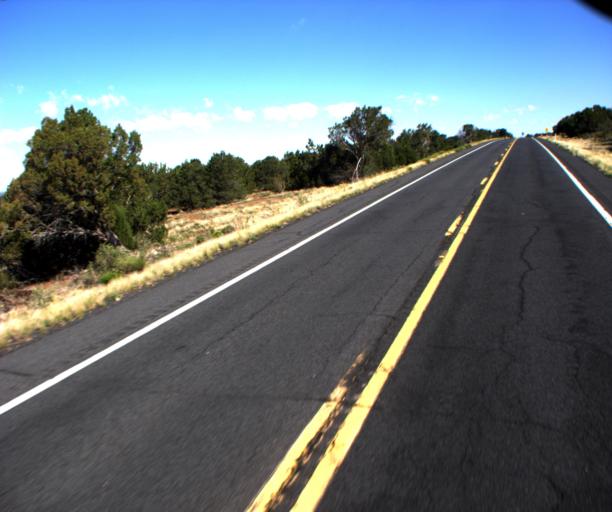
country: US
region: Arizona
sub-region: Coconino County
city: Williams
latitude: 35.3946
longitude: -112.1678
